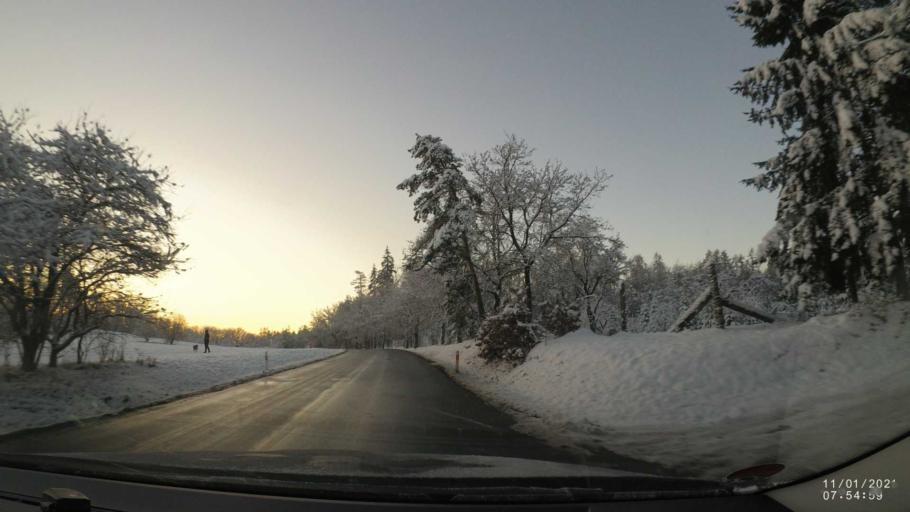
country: CZ
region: South Moravian
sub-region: Okres Blansko
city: Adamov
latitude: 49.2845
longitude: 16.6322
